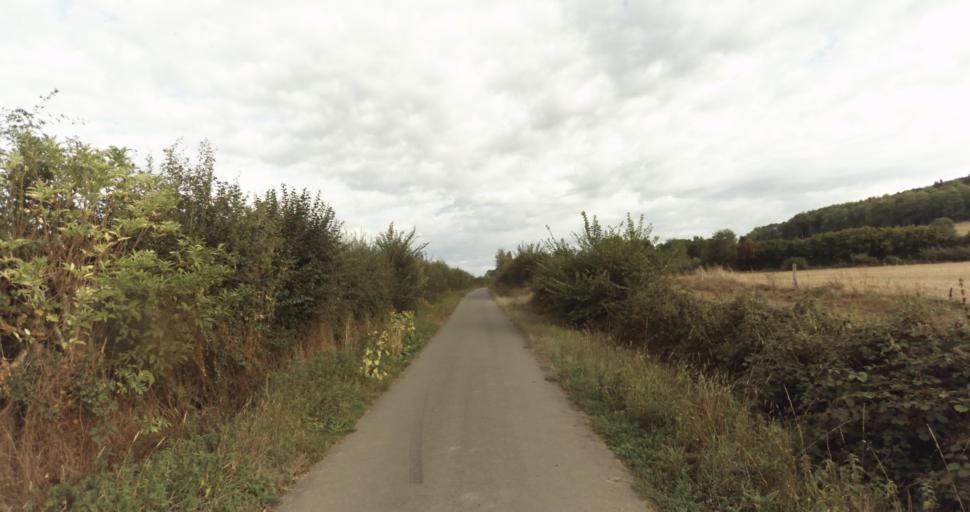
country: FR
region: Lower Normandy
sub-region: Departement de l'Orne
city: Vimoutiers
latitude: 48.9455
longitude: 0.2737
